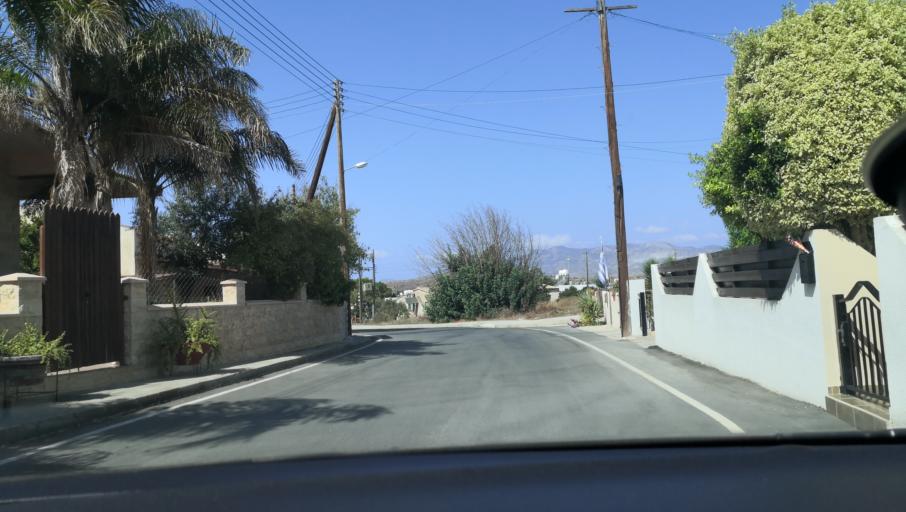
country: CY
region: Lefkosia
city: Mammari
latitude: 35.1736
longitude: 33.2070
